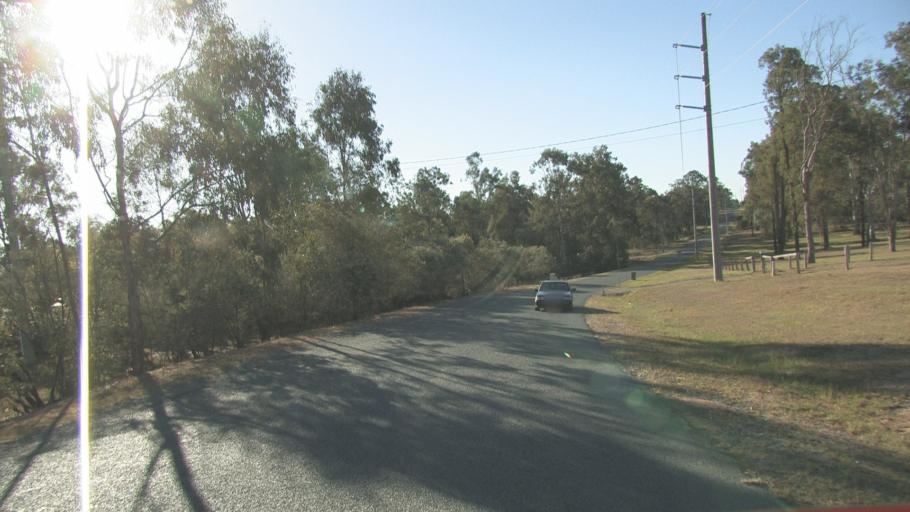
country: AU
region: Queensland
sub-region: Logan
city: North Maclean
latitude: -27.8041
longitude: 153.0407
